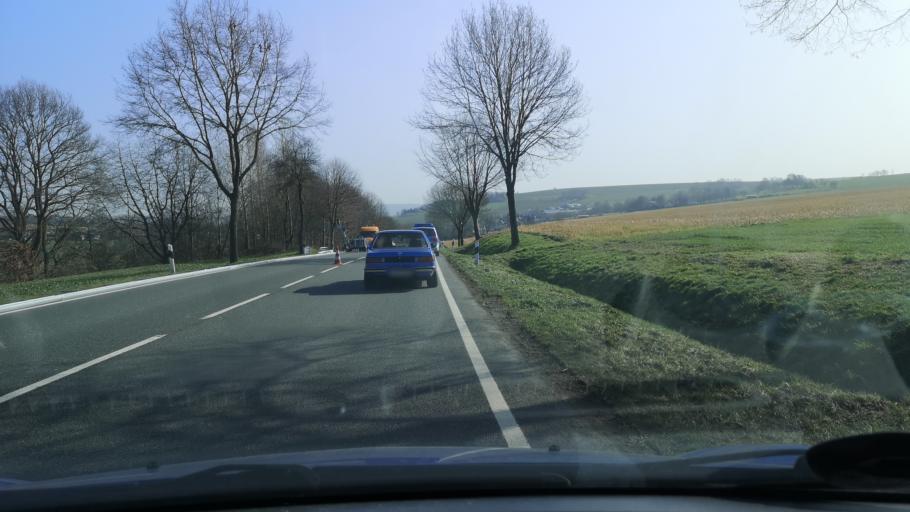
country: DE
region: Lower Saxony
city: Bodenfelde
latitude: 51.6744
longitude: 9.5859
